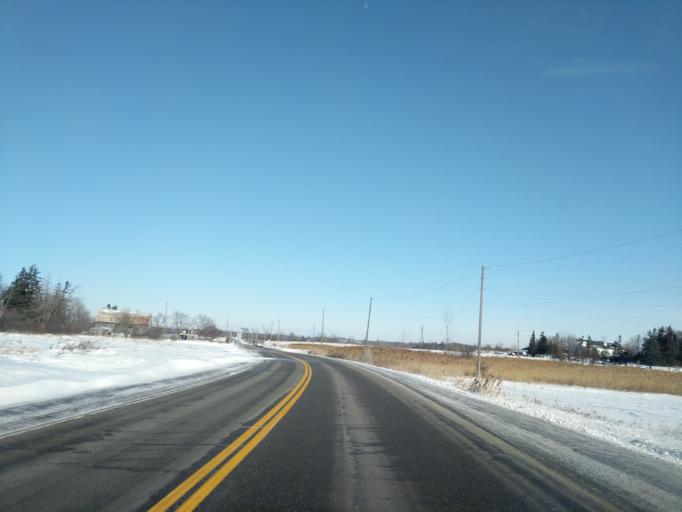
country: CA
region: Ontario
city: Pickering
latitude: 43.8550
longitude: -79.1312
